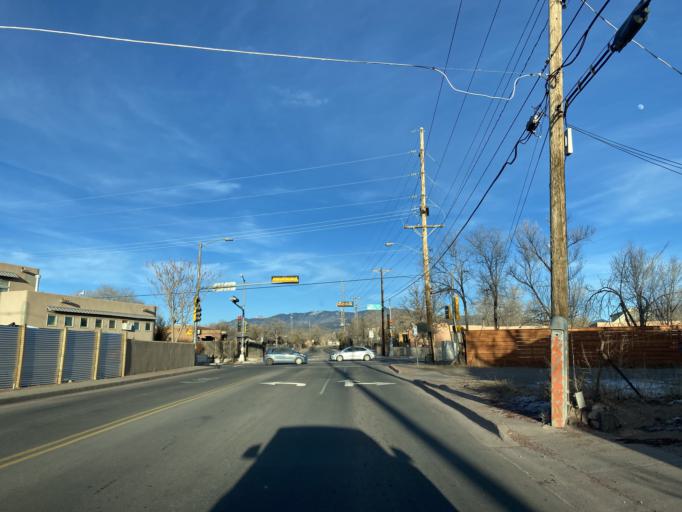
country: US
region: New Mexico
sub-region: Santa Fe County
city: Santa Fe
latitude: 35.6808
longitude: -105.9640
